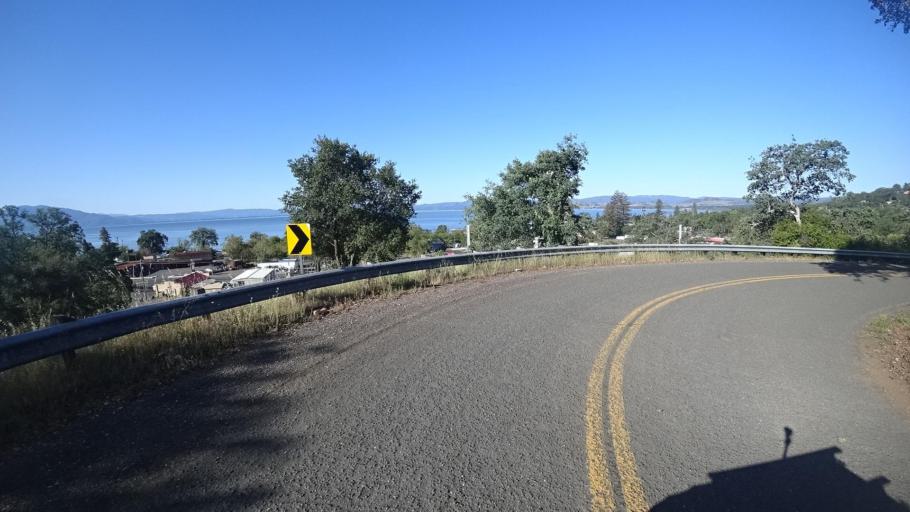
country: US
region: California
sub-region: Lake County
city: Nice
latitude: 39.1239
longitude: -122.8422
